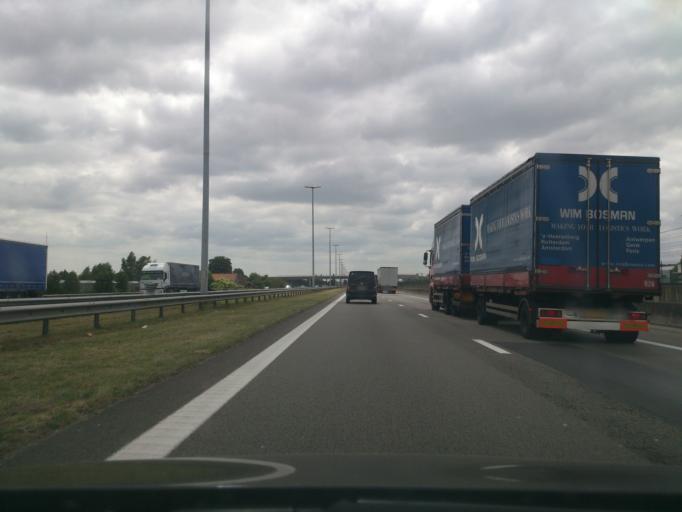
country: NL
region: North Brabant
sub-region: Gemeente Zundert
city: Zundert
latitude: 51.4642
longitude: 4.7253
